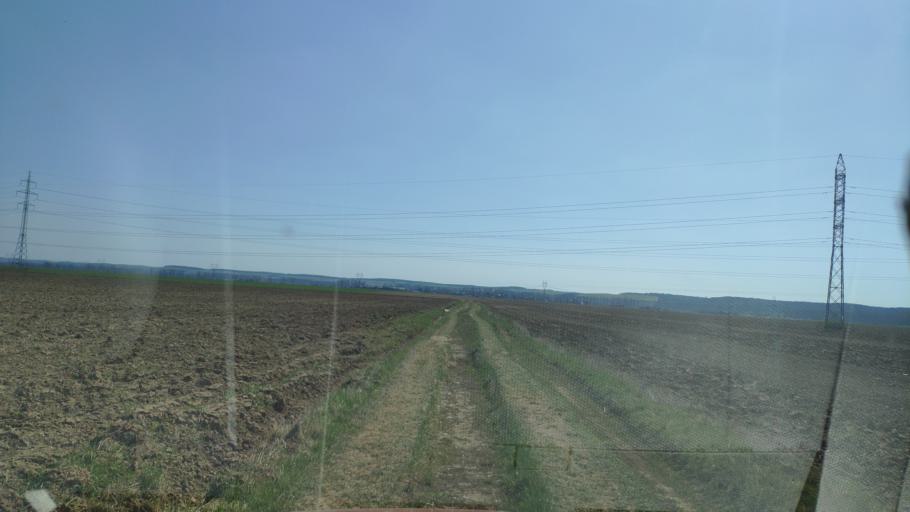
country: SK
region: Kosicky
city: Moldava nad Bodvou
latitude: 48.5996
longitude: 20.9452
